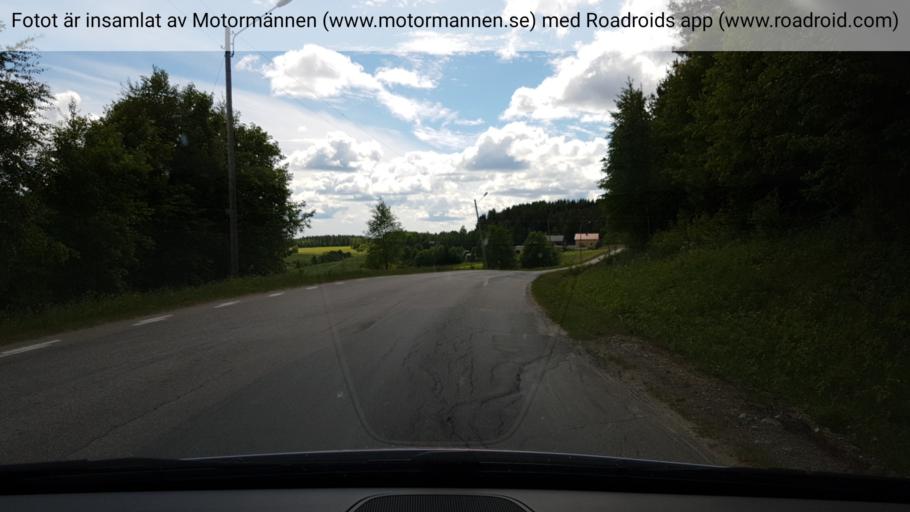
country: SE
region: Vaesterbotten
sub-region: Umea Kommun
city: Roback
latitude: 64.0323
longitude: 20.0838
